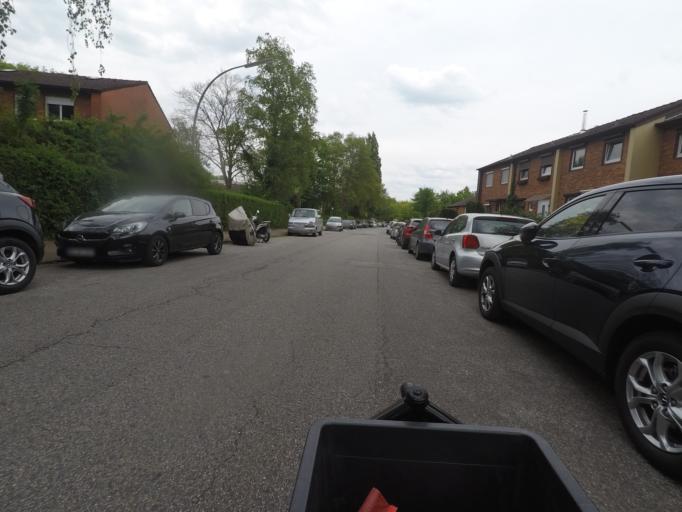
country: DE
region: Hamburg
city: Steilshoop
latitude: 53.6066
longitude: 10.0855
